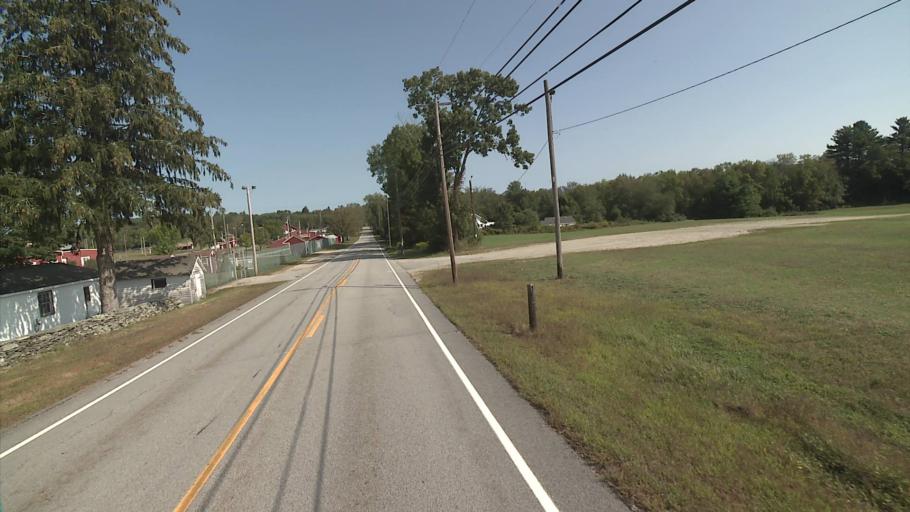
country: US
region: Connecticut
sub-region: Windham County
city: Wauregan
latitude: 41.7781
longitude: -71.9521
